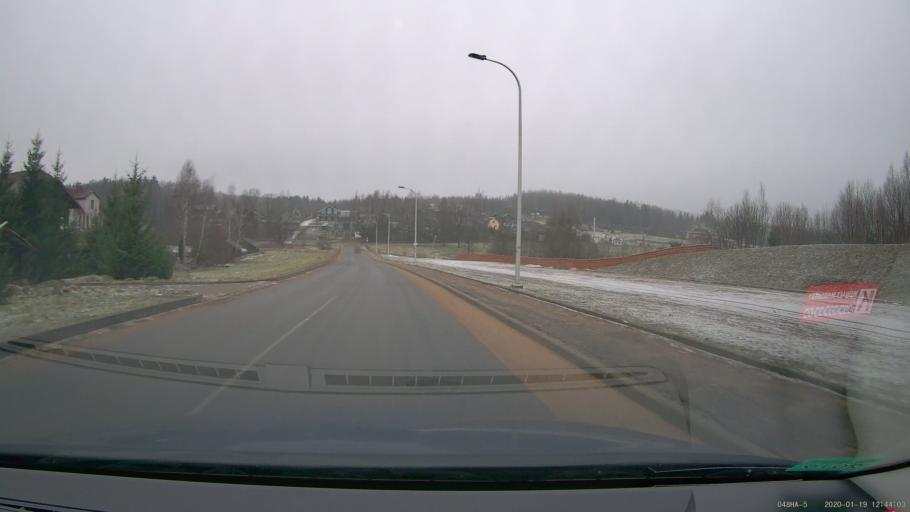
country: BY
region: Minsk
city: Lahoysk
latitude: 54.1790
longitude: 27.8087
